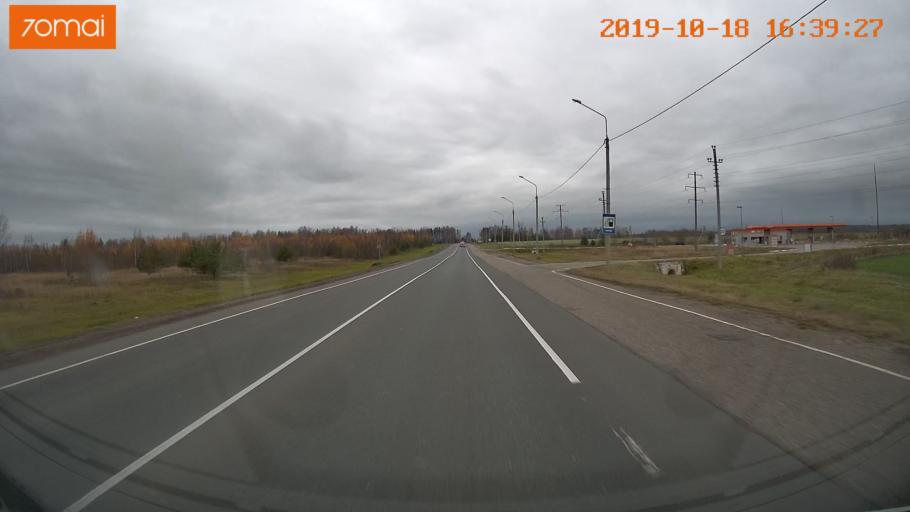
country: RU
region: Vladimir
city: Suzdal'
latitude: 56.4513
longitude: 40.4617
